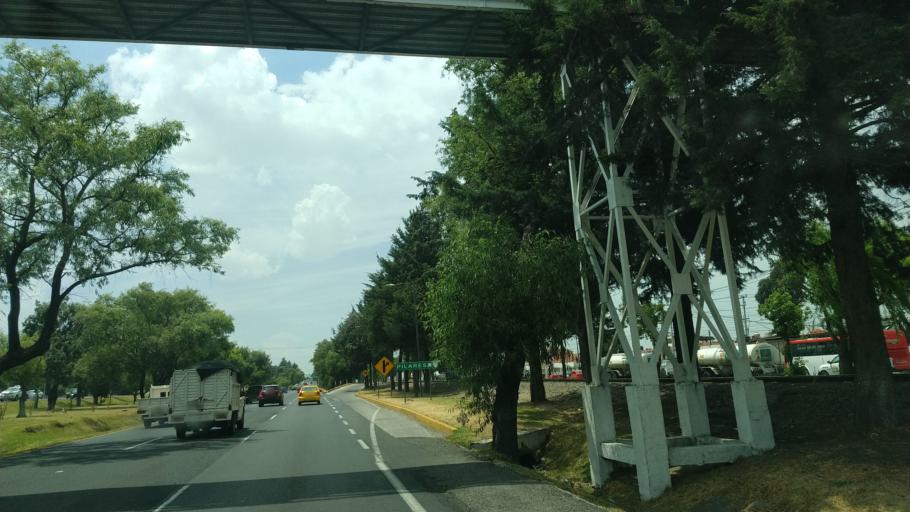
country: MX
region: Mexico
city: Santa Maria Totoltepec
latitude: 19.2869
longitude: -99.5934
